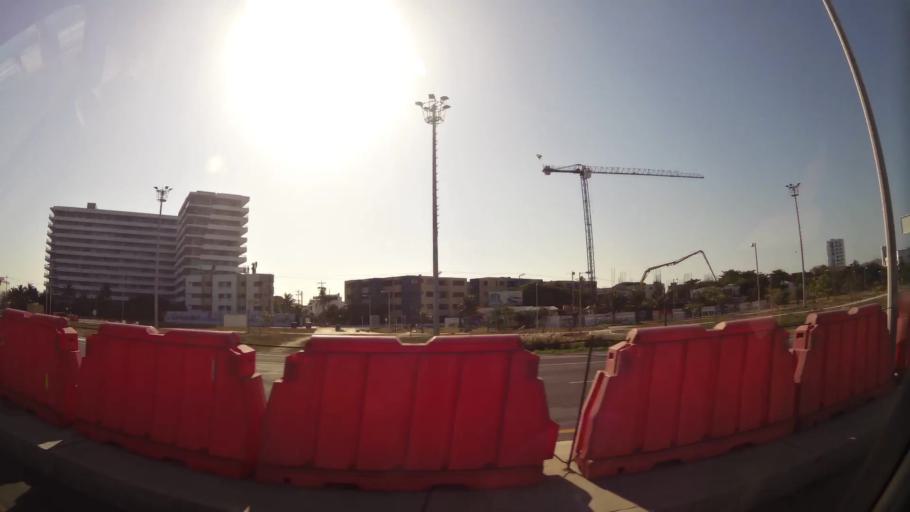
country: CO
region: Bolivar
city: Cartagena
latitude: 10.4507
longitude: -75.5178
